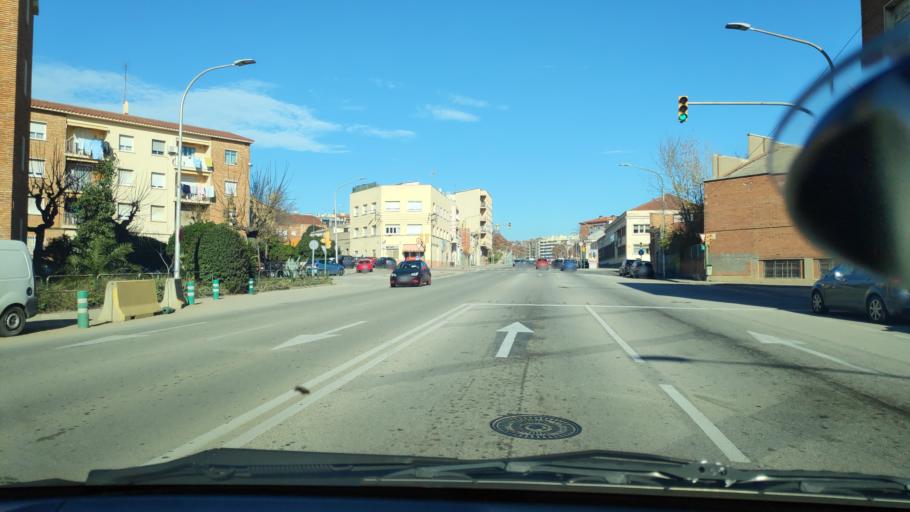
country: ES
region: Catalonia
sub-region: Provincia de Barcelona
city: Sabadell
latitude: 41.5395
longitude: 2.0975
